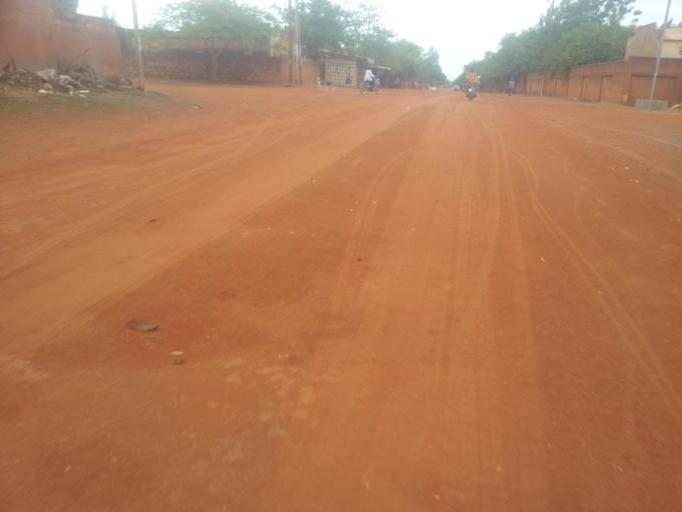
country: BF
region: Centre
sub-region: Kadiogo Province
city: Ouagadougou
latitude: 12.3827
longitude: -1.5453
